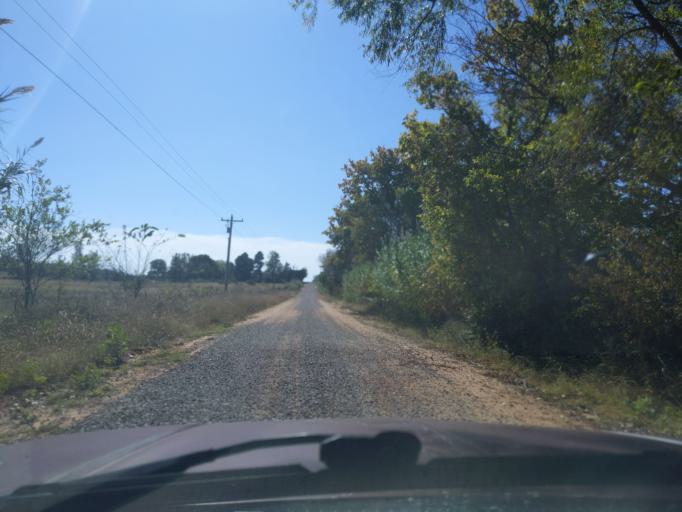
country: US
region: Oklahoma
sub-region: Creek County
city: Bristow
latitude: 35.6639
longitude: -96.4234
